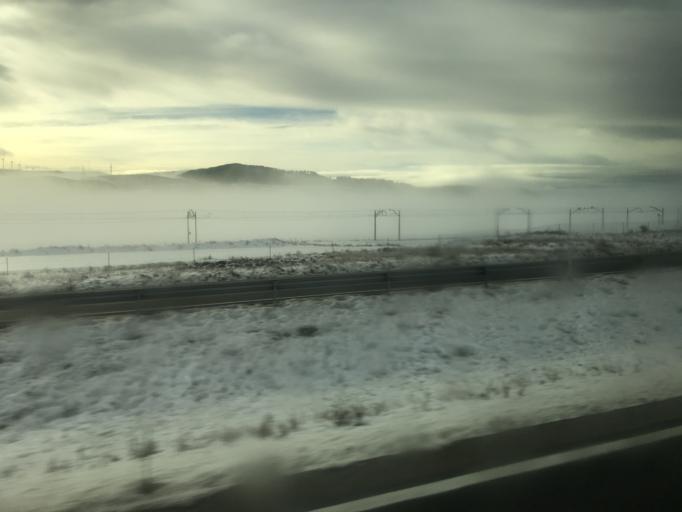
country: ES
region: Castille and Leon
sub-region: Provincia de Burgos
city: Santa Olalla de Bureba
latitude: 42.4716
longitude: -3.4443
